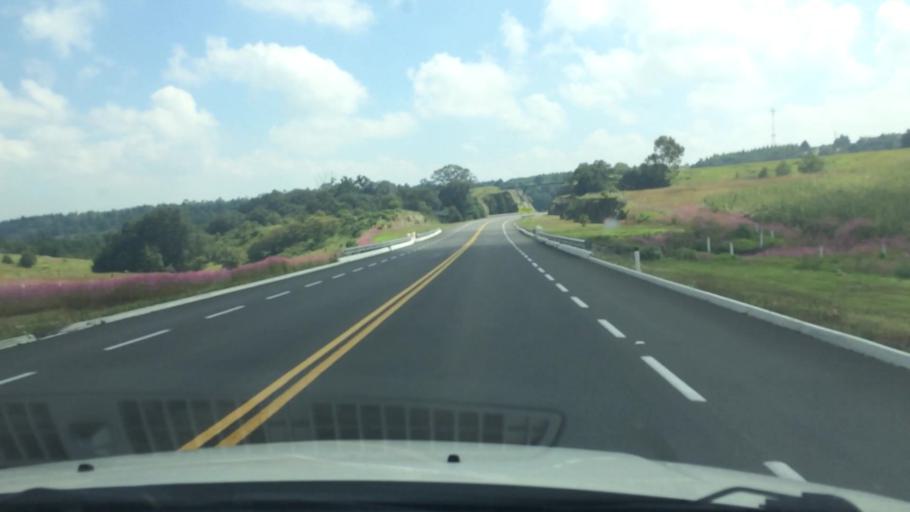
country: MX
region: Mexico
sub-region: Villa Victoria
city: Colonia Doctor Gustavo Baz
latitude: 19.3752
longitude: -99.9096
